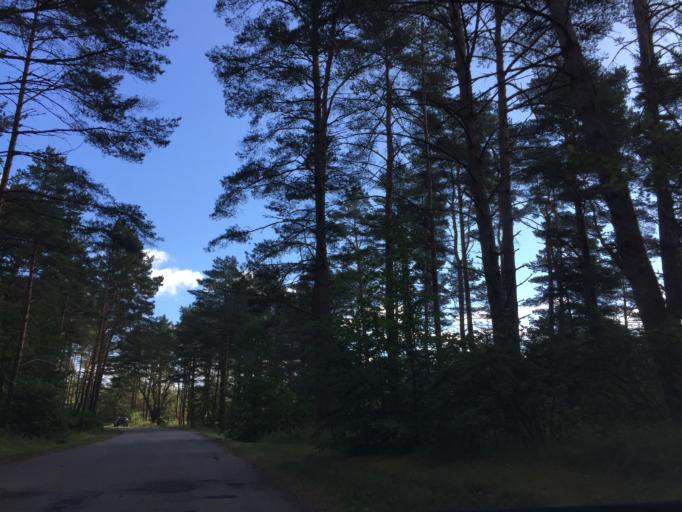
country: LV
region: Ventspils
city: Ventspils
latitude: 57.4431
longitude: 21.6192
